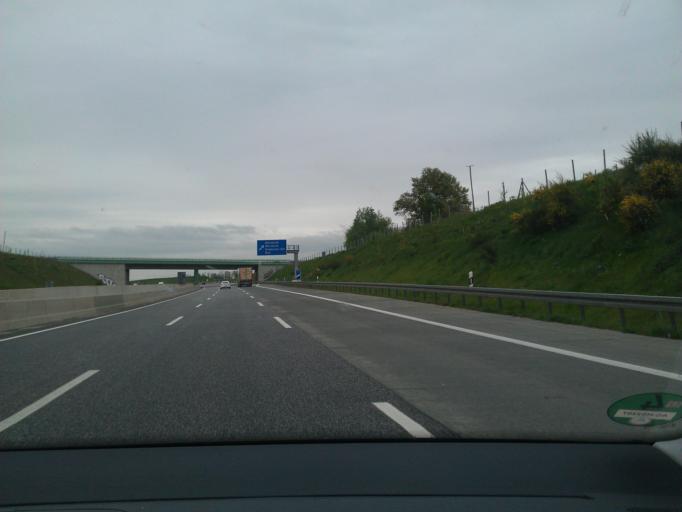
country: DE
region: North Rhine-Westphalia
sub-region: Regierungsbezirk Koln
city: Merzenich
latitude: 50.8490
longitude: 6.5121
